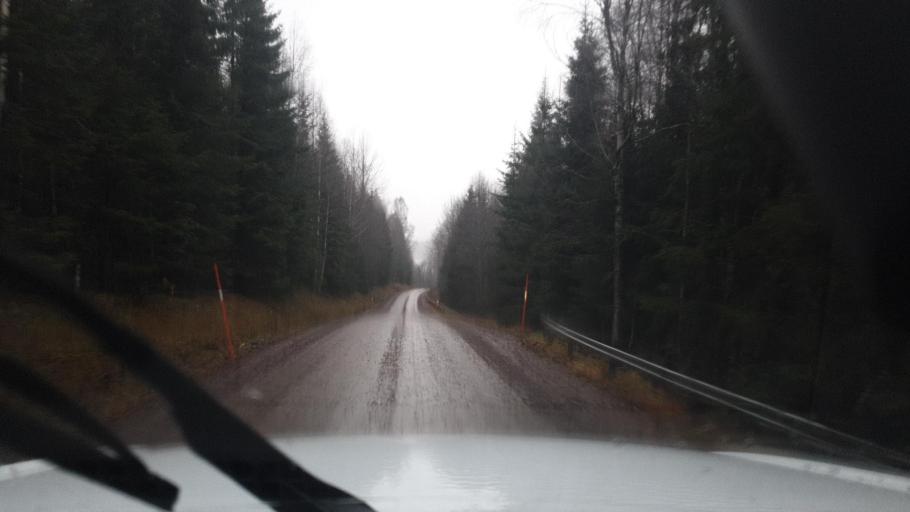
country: SE
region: Vaermland
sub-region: Arvika Kommun
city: Arvika
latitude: 60.0122
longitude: 12.6485
